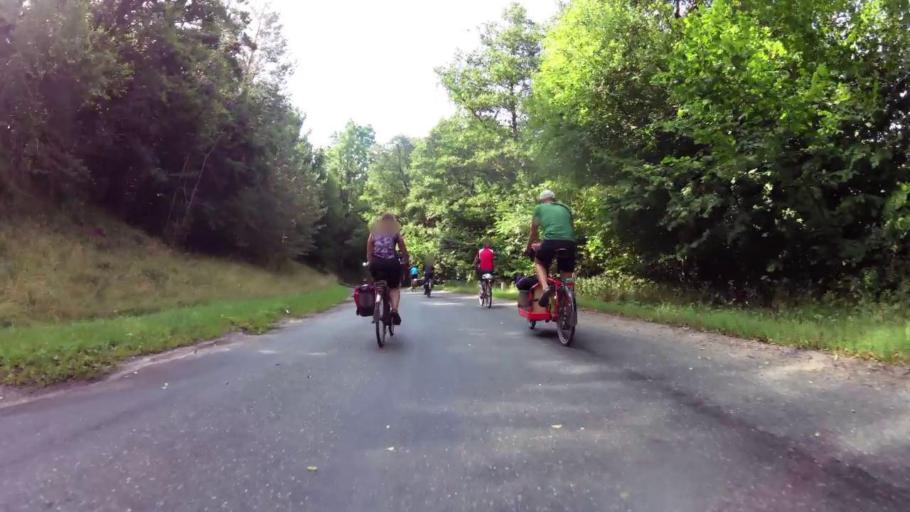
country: PL
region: West Pomeranian Voivodeship
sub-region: Powiat drawski
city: Drawsko Pomorskie
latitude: 53.4761
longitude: 15.7775
